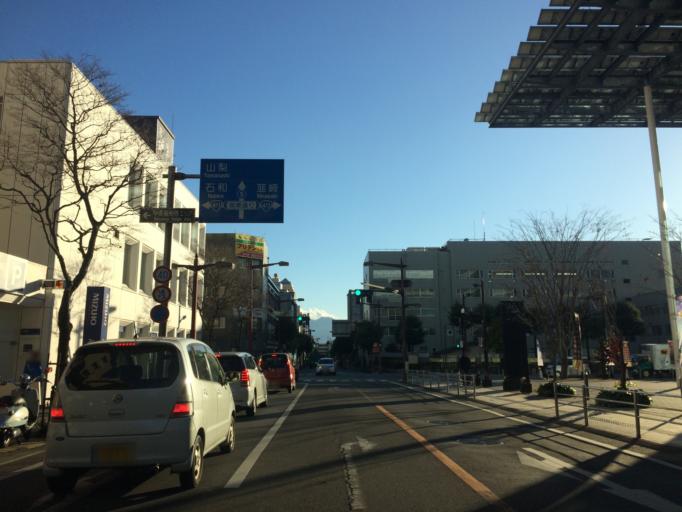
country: JP
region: Yamanashi
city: Kofu-shi
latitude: 35.6621
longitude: 138.5688
